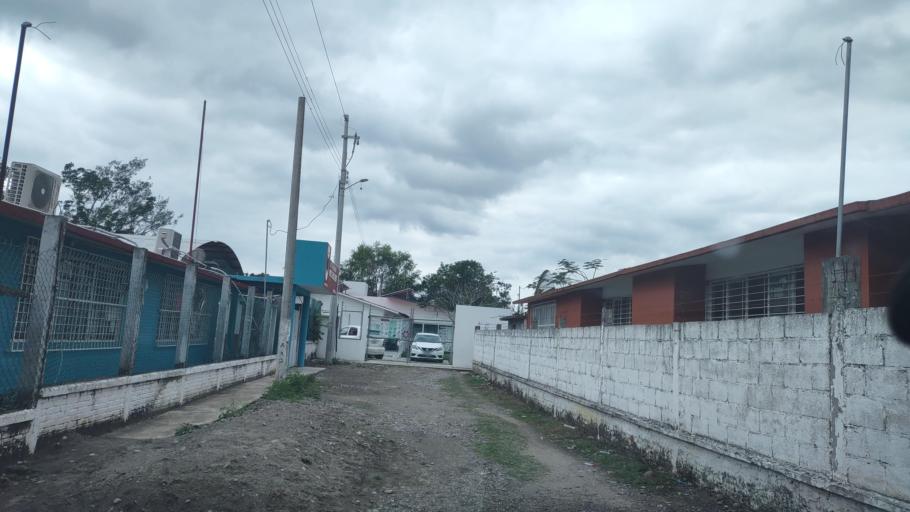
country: MX
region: Veracruz
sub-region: Papantla
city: Polutla
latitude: 20.4676
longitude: -97.2561
